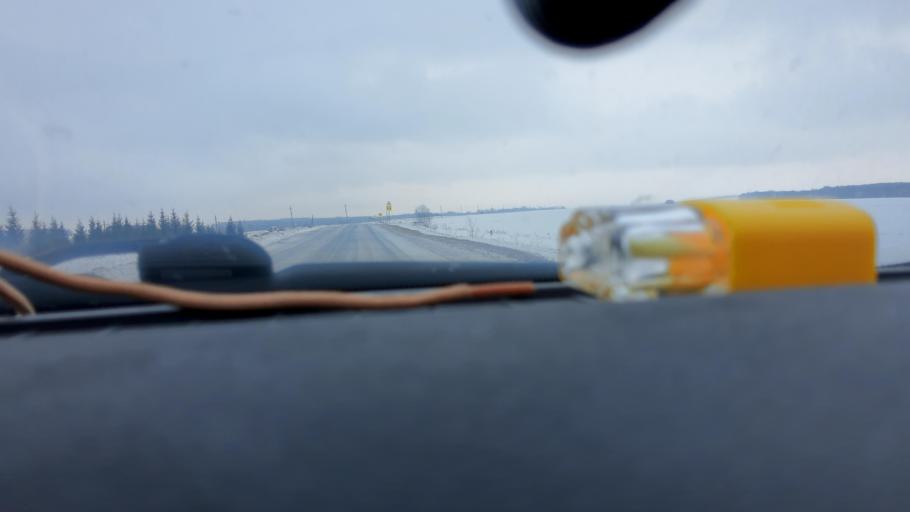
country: RU
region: Bashkortostan
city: Iglino
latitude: 54.7115
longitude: 56.4007
